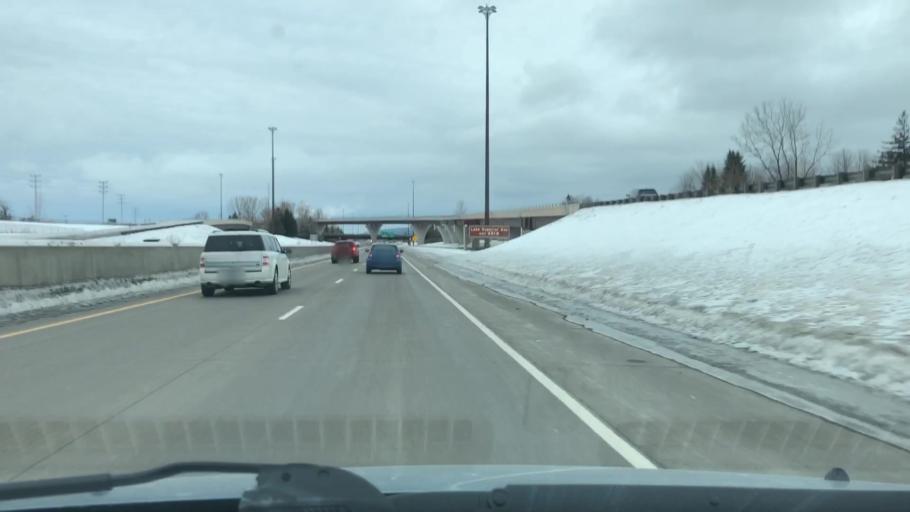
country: US
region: Wisconsin
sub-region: Douglas County
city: Superior
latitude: 46.7463
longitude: -92.1499
